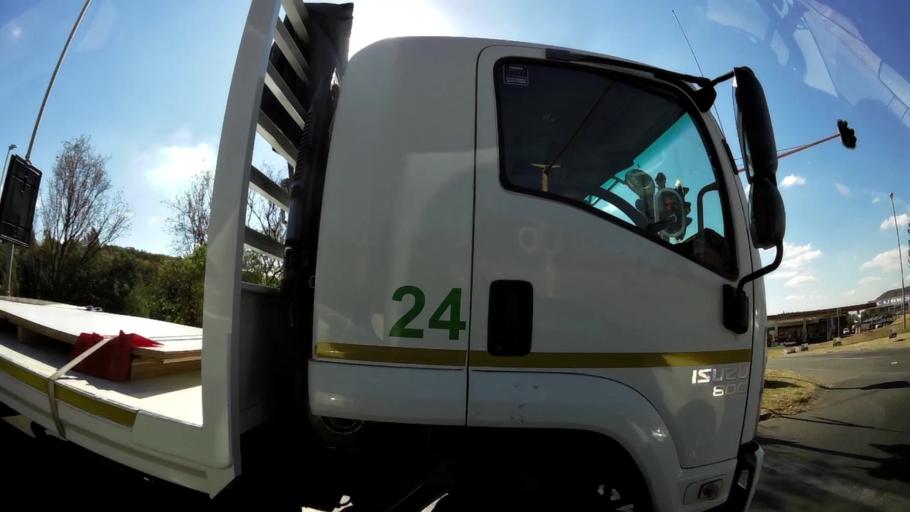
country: ZA
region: Gauteng
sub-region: West Rand District Municipality
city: Krugersdorp
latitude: -26.0928
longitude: 27.8255
